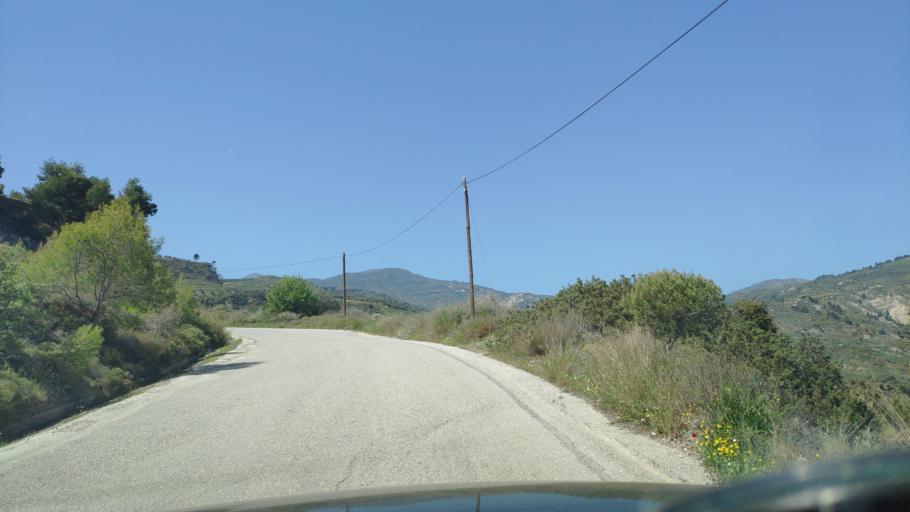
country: GR
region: West Greece
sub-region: Nomos Achaias
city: Aiyira
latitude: 38.1292
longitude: 22.3448
